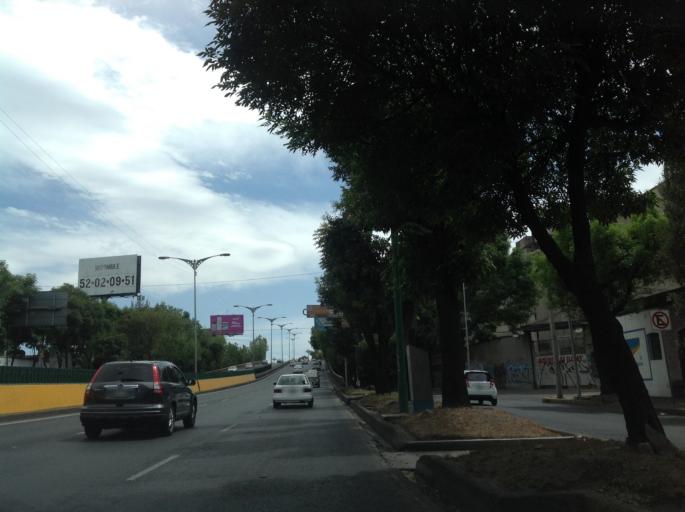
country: MX
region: Mexico City
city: Azcapotzalco
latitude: 19.4650
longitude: -99.1901
